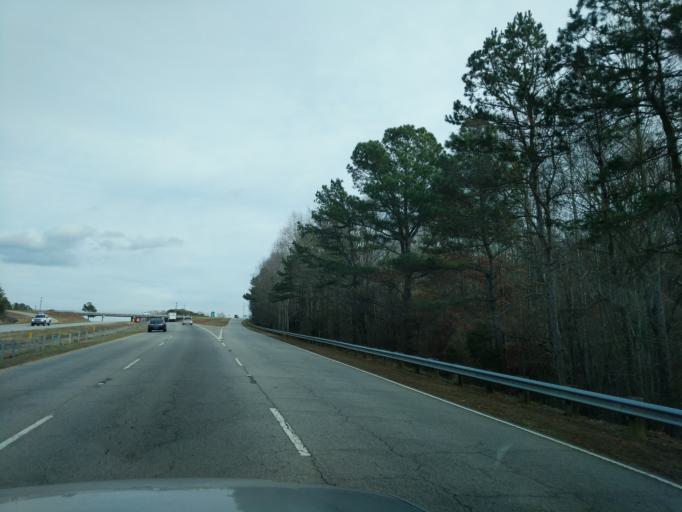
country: US
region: South Carolina
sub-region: Anderson County
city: Pendleton
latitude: 34.6869
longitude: -82.7967
